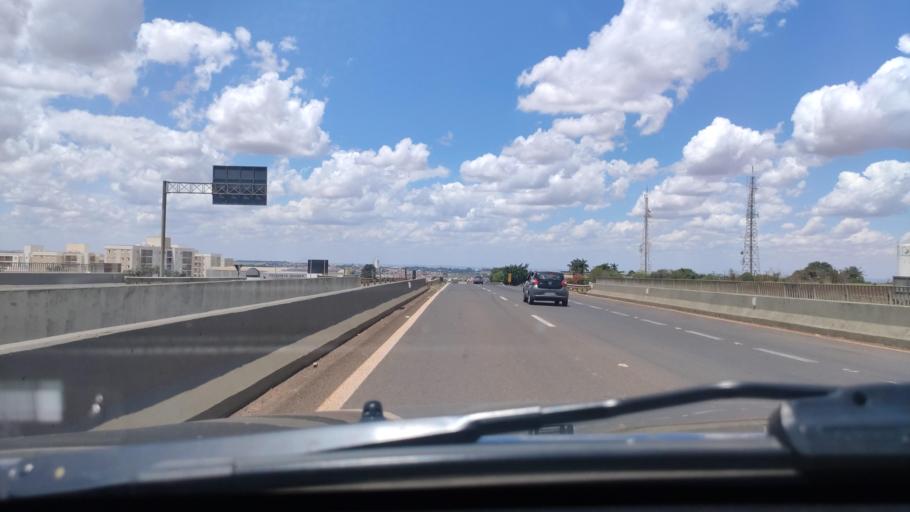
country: BR
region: Sao Paulo
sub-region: Jau
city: Jau
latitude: -22.2566
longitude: -48.5510
